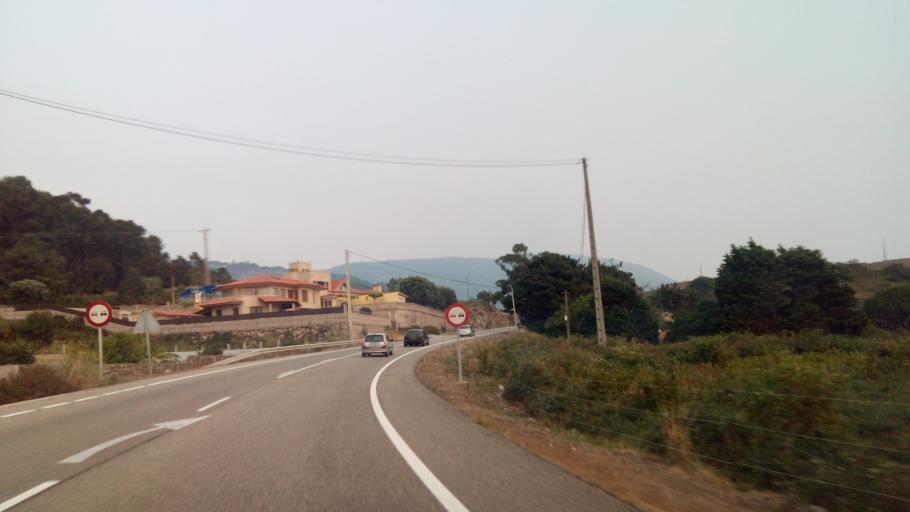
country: ES
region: Galicia
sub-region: Provincia de Pontevedra
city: Oia
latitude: 42.0566
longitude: -8.8877
